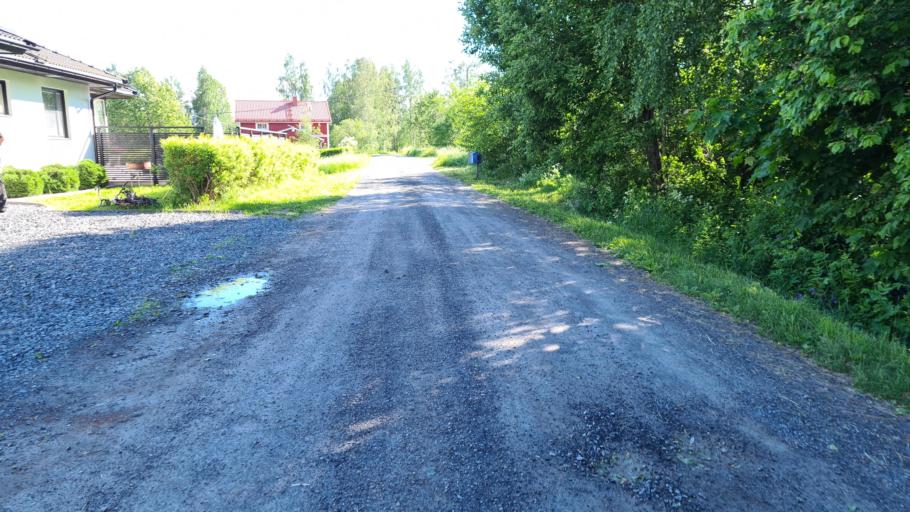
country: SE
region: Vaesternorrland
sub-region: Kramfors Kommun
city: Nordingra
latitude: 63.0619
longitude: 18.3498
